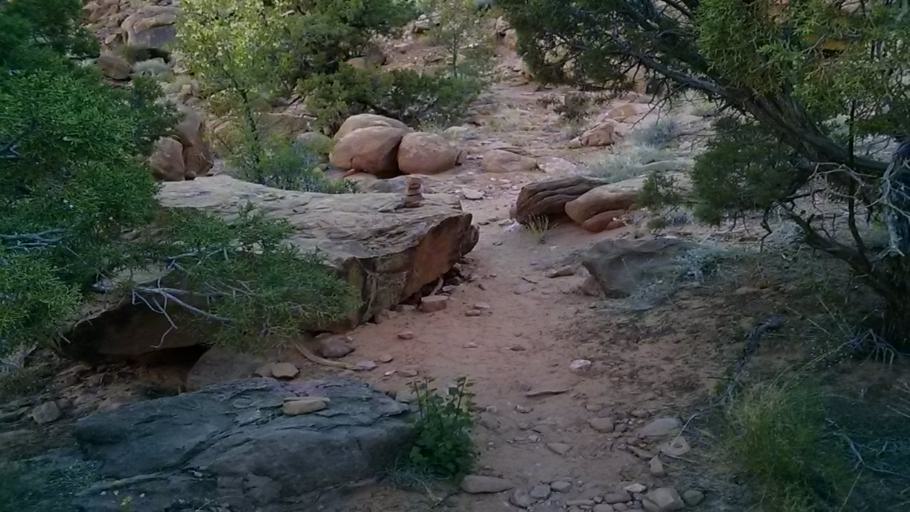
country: US
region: Utah
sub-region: Grand County
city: Moab
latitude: 38.4314
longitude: -109.9494
